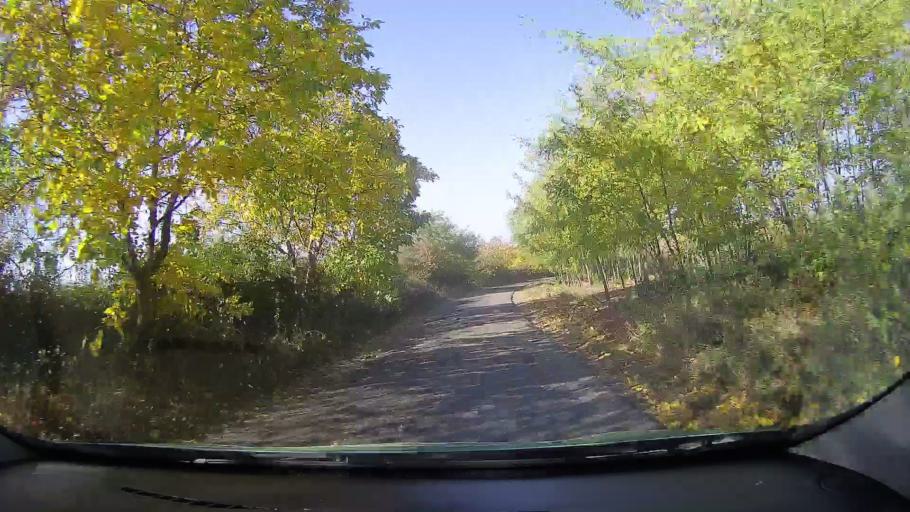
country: RO
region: Satu Mare
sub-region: Comuna Sauca
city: Sauca
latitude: 47.4684
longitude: 22.5053
